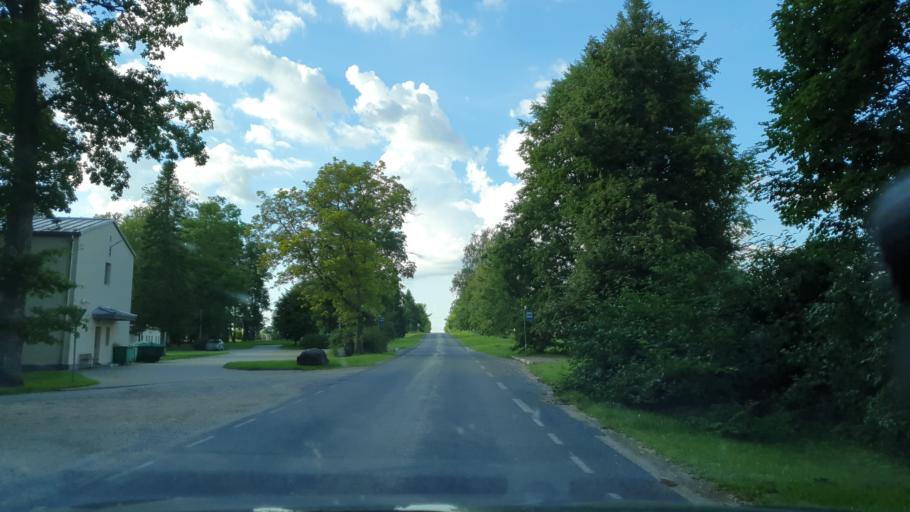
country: EE
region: Jogevamaa
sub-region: Tabivere vald
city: Tabivere
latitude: 58.6554
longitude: 26.6041
